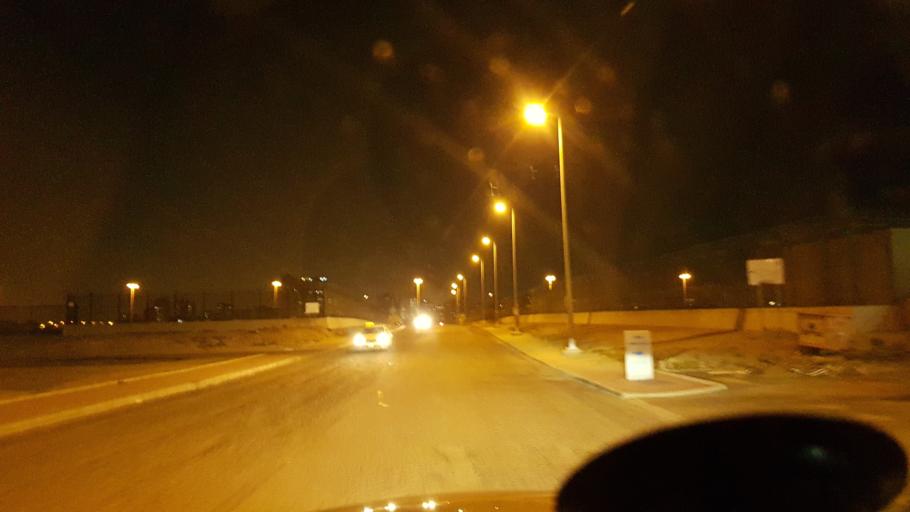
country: KW
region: Al Ahmadi
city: Al Manqaf
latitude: 29.1180
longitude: 48.1289
